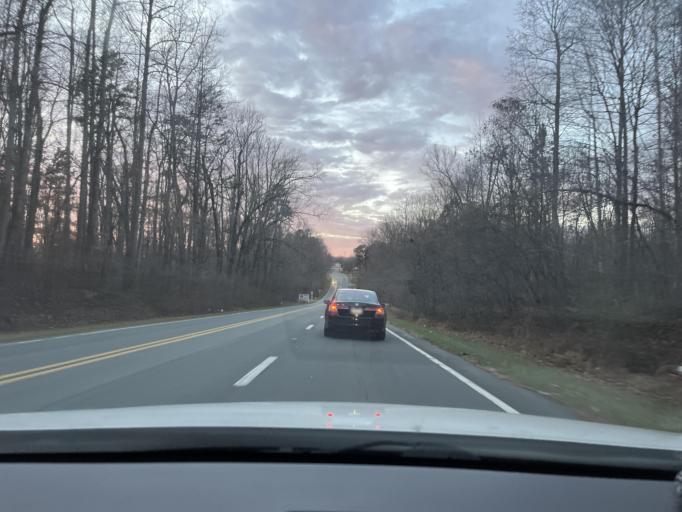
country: US
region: North Carolina
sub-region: Guilford County
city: McLeansville
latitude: 36.0832
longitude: -79.6498
